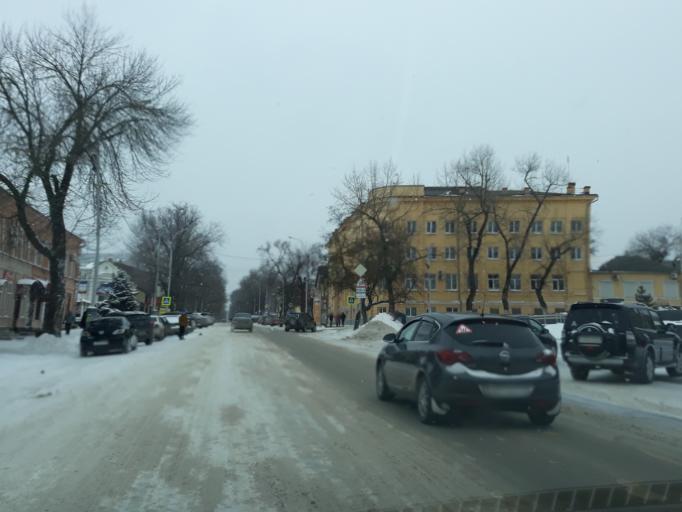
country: RU
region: Rostov
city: Taganrog
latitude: 47.2159
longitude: 38.9285
